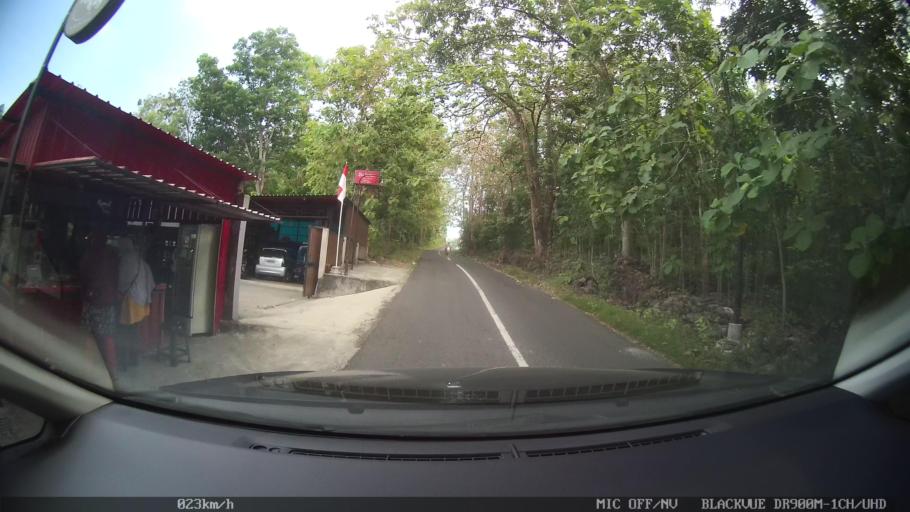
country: ID
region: Daerah Istimewa Yogyakarta
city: Bantul
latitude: -7.8601
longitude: 110.3081
